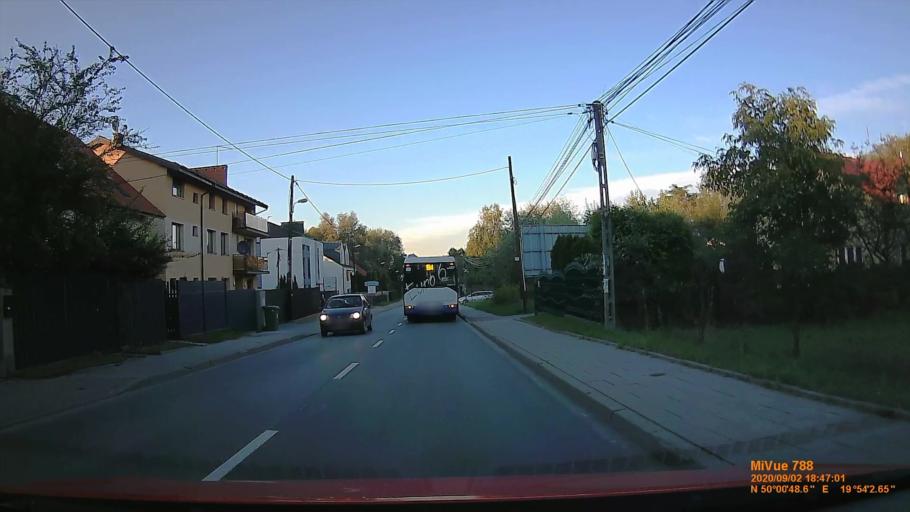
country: PL
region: Lesser Poland Voivodeship
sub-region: Krakow
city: Sidzina
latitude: 50.0137
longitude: 19.9009
